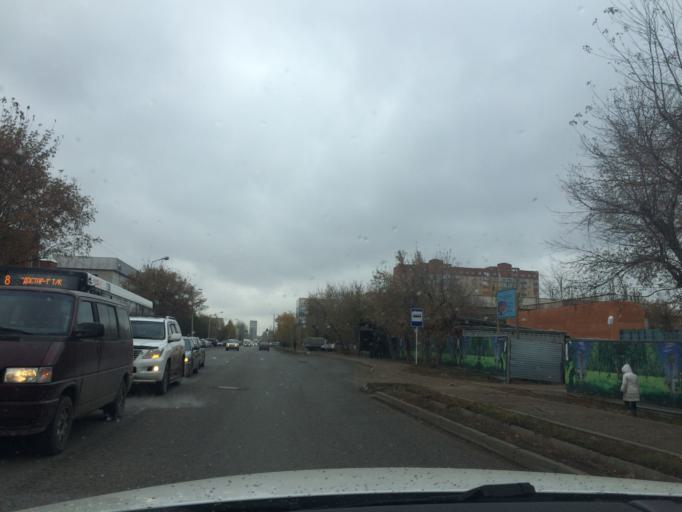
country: KZ
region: Astana Qalasy
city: Astana
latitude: 51.1704
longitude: 71.4509
